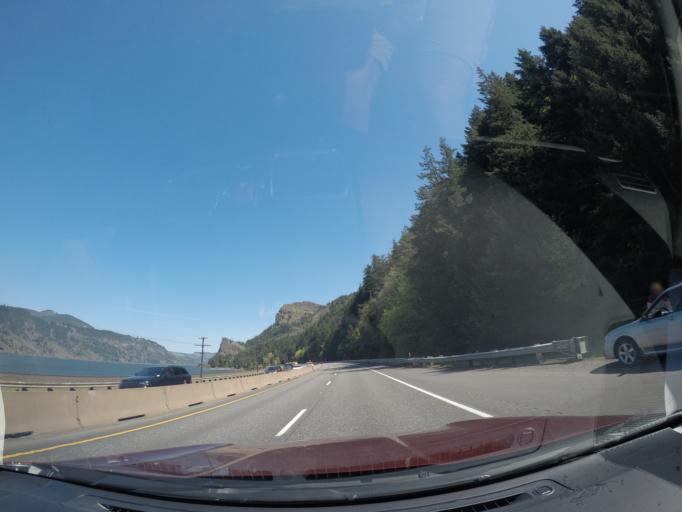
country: US
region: Oregon
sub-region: Hood River County
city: Hood River
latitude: 45.6993
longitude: -121.6349
